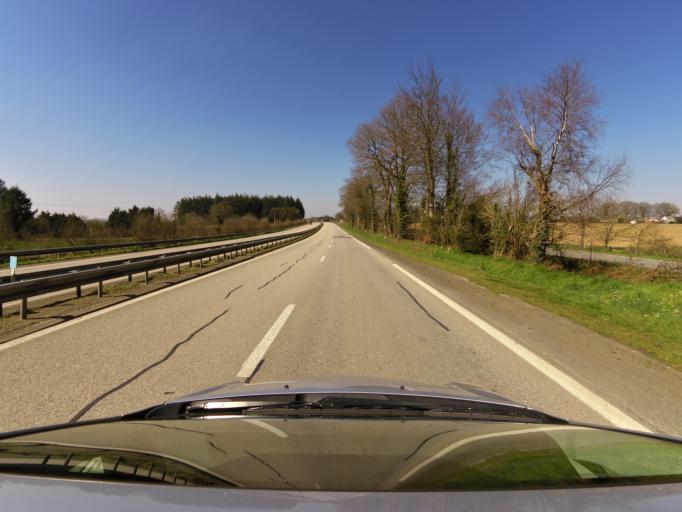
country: FR
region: Brittany
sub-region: Departement du Morbihan
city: Plumelin
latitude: 47.8953
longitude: -2.9028
